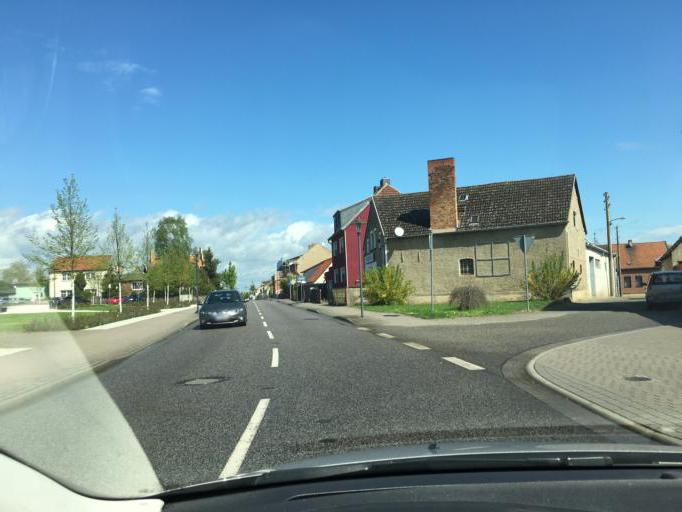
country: DE
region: Saxony-Anhalt
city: Haldensleben I
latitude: 52.2665
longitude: 11.4214
